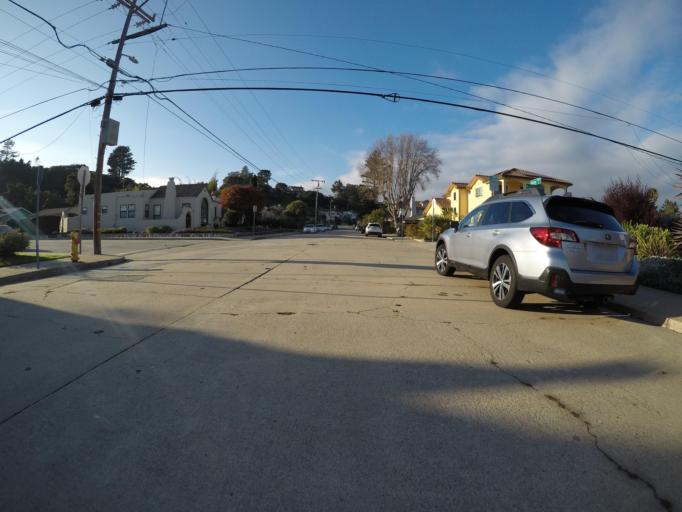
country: US
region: California
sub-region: Santa Cruz County
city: Santa Cruz
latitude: 36.9674
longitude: -122.0451
